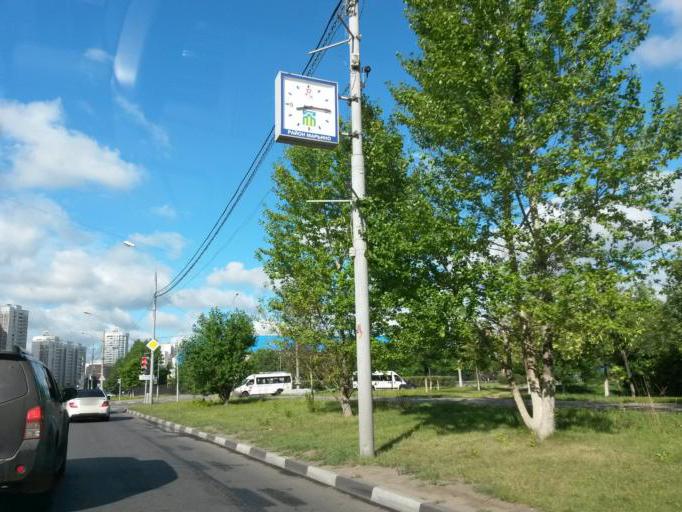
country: RU
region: Moscow
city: Brateyevo
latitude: 55.6540
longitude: 37.7564
